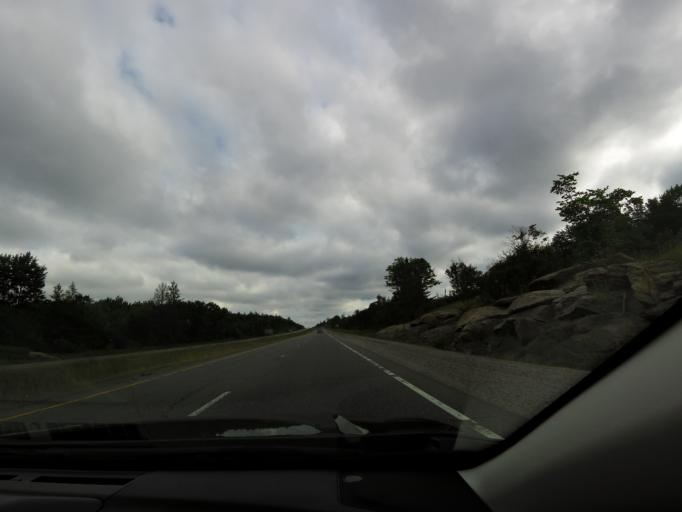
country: CA
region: Ontario
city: Gravenhurst
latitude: 44.9551
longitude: -79.3298
